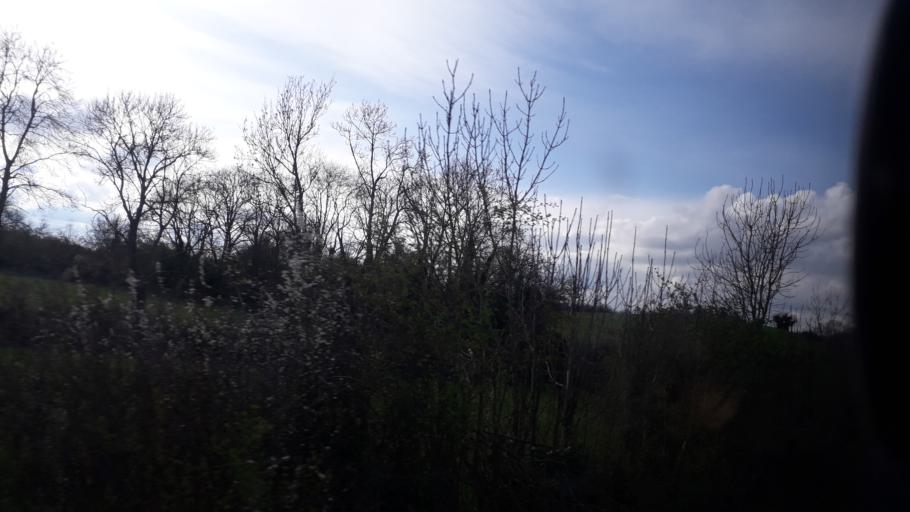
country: IE
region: Leinster
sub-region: An Mhi
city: Longwood
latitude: 53.4613
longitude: -6.9667
